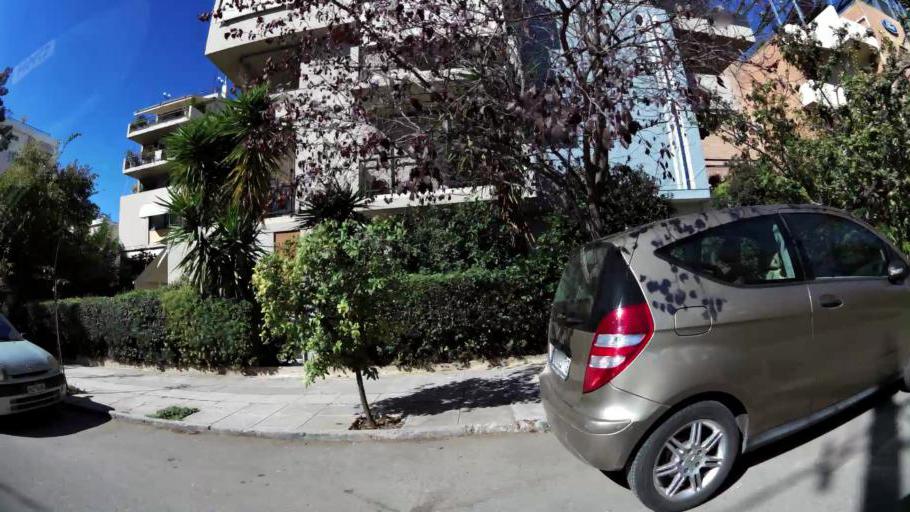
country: GR
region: Attica
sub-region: Nomarchia Athinas
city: Khalandrion
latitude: 38.0326
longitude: 23.8109
